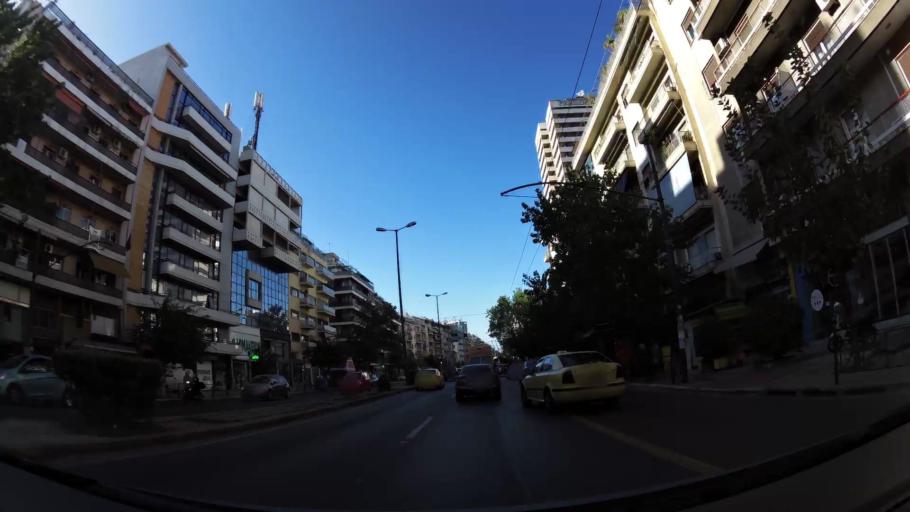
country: GR
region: Attica
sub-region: Nomarchia Athinas
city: Psychiko
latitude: 37.9895
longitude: 23.7647
